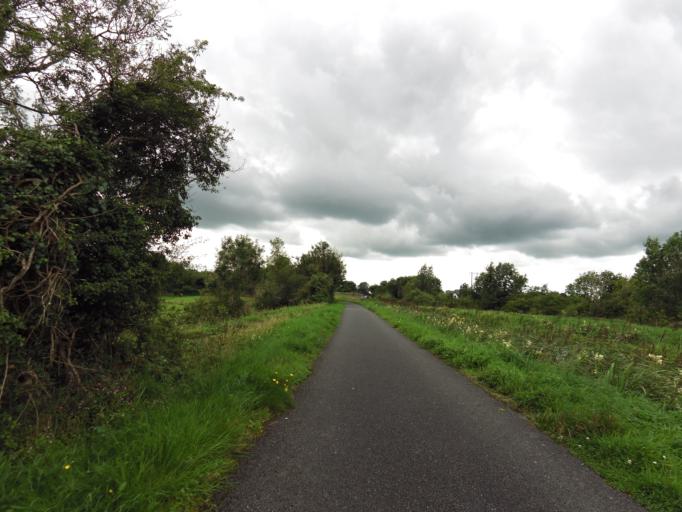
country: IE
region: Leinster
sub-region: An Iarmhi
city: An Muileann gCearr
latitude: 53.5108
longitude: -7.3841
